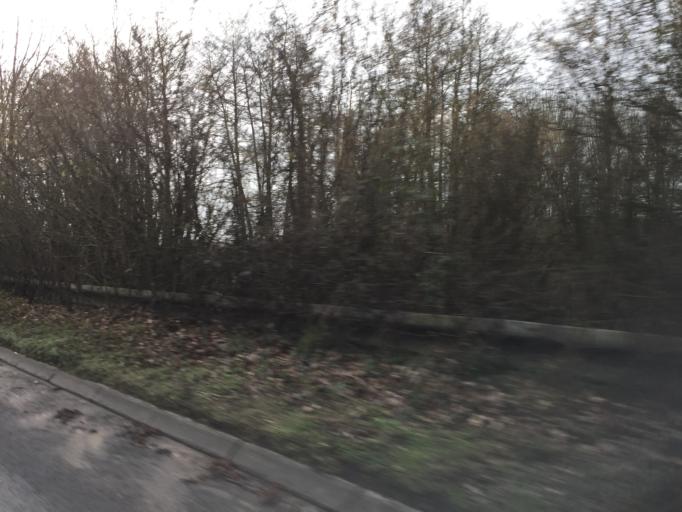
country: GB
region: England
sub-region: West Berkshire
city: Pangbourne
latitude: 51.4592
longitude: -1.0902
